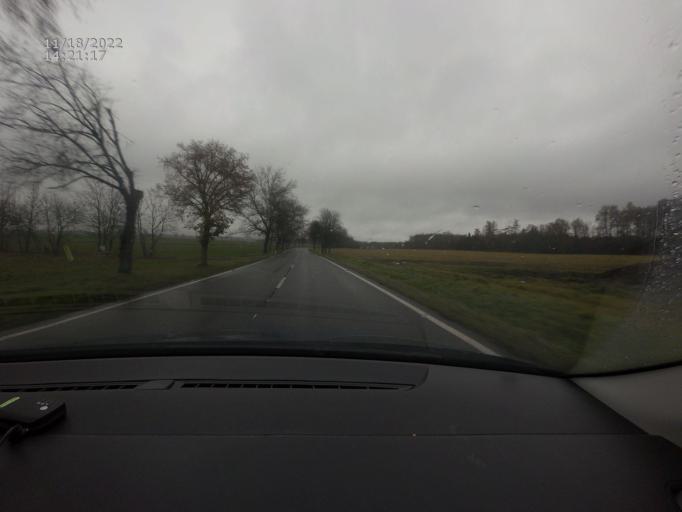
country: CZ
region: Jihocesky
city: Cimelice
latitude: 49.4417
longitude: 14.0887
